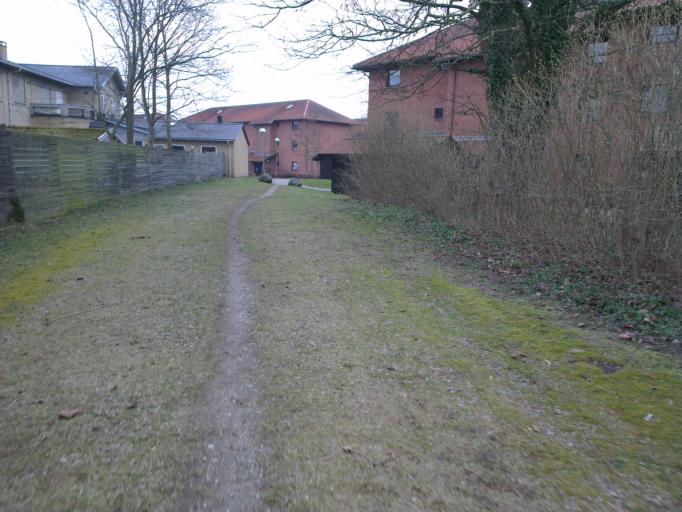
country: DK
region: Capital Region
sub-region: Frederikssund Kommune
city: Frederikssund
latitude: 55.8415
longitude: 12.0559
